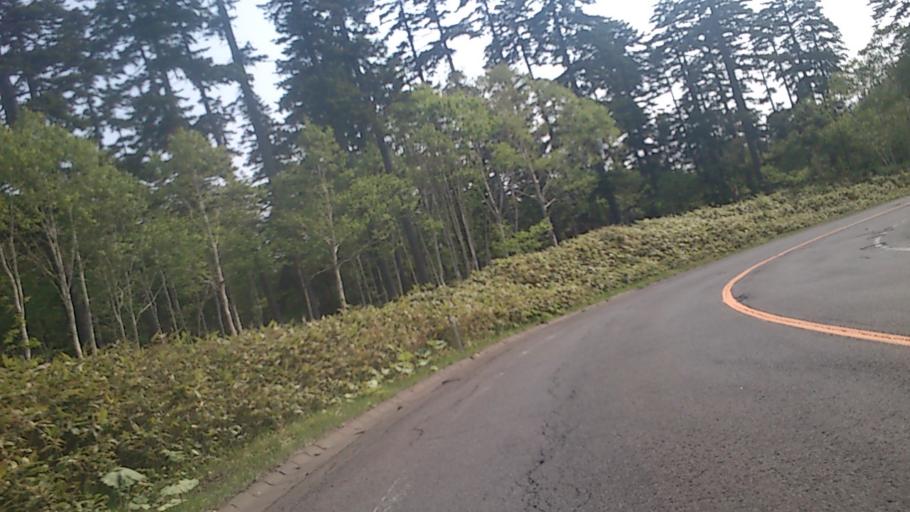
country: JP
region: Hokkaido
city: Bihoro
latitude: 43.4606
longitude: 144.2261
